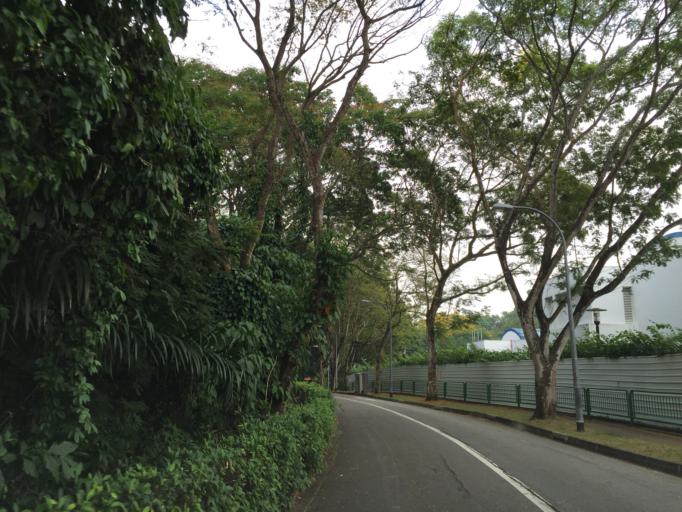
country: SG
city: Singapore
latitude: 1.3238
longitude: 103.8293
